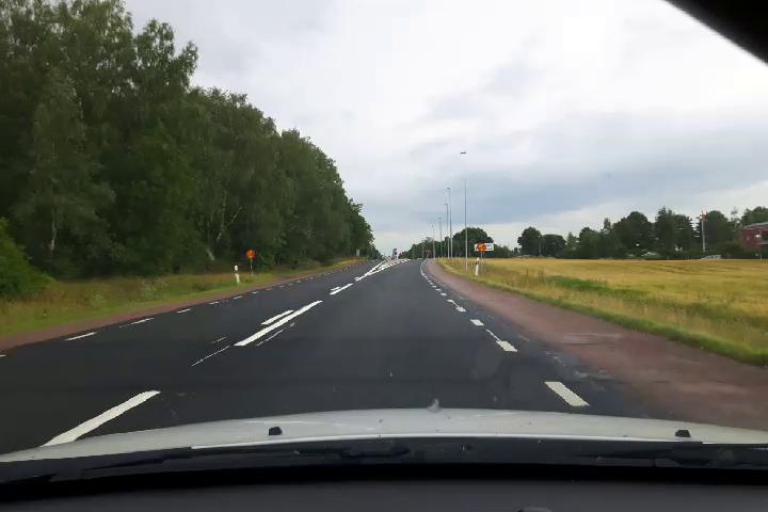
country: SE
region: Uppsala
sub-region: Uppsala Kommun
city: Gamla Uppsala
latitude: 59.8841
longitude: 17.6202
